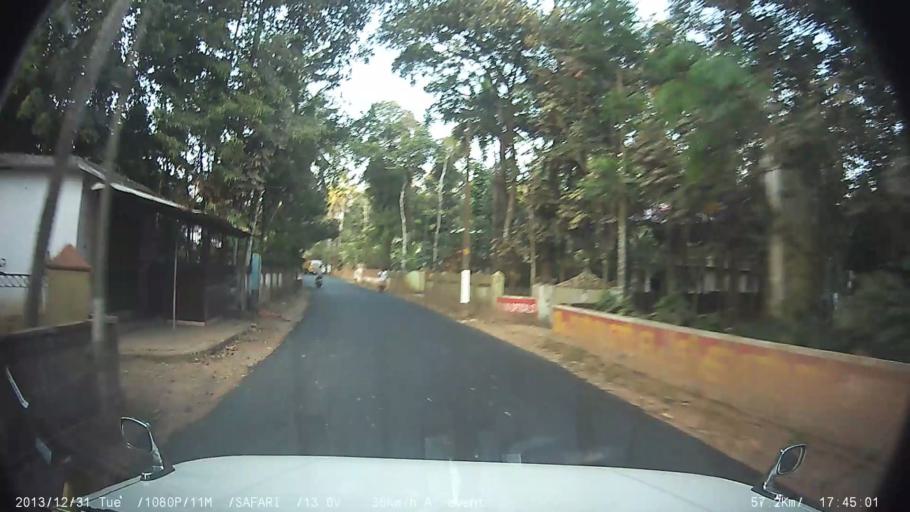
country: IN
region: Kerala
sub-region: Kottayam
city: Vaikam
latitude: 9.7287
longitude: 76.4777
